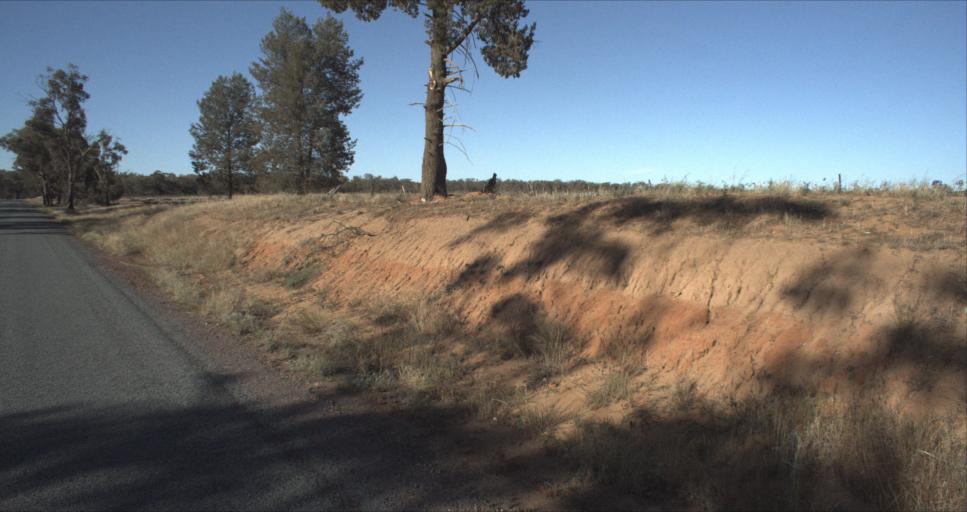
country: AU
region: New South Wales
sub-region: Leeton
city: Leeton
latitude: -34.6480
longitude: 146.3518
